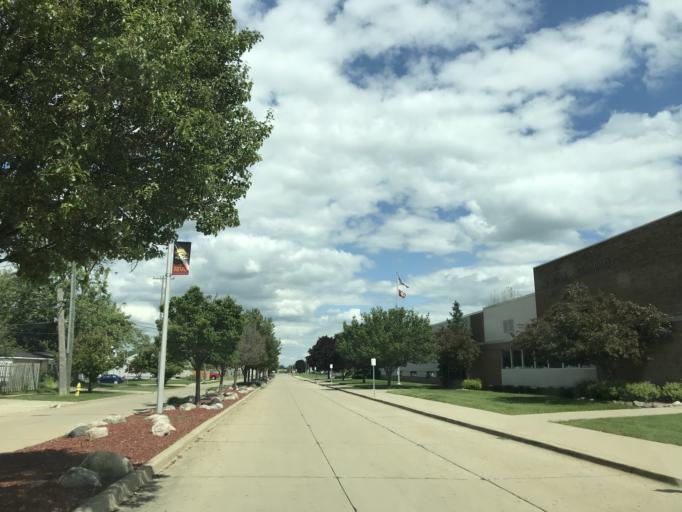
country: US
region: Michigan
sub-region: Wayne County
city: Riverview
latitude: 42.1778
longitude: -83.1779
